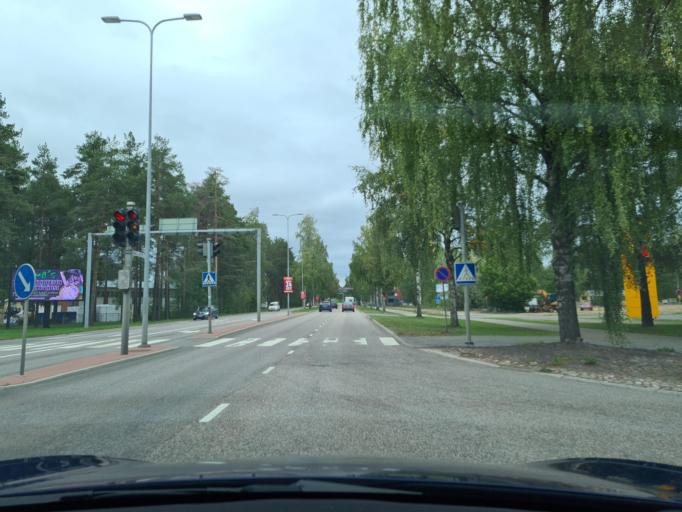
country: FI
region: South Karelia
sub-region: Lappeenranta
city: Lappeenranta
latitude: 61.0450
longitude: 28.1793
